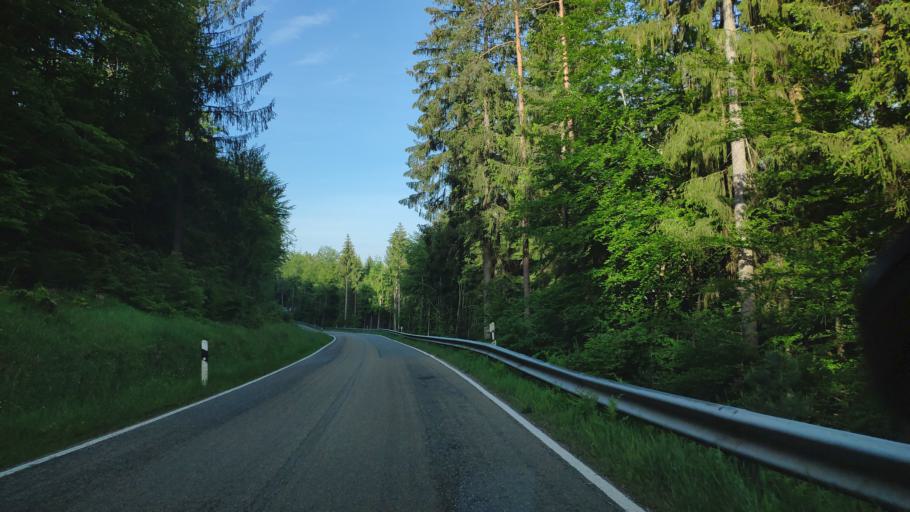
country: DE
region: Rheinland-Pfalz
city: Lemberg
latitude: 49.1428
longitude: 7.6931
